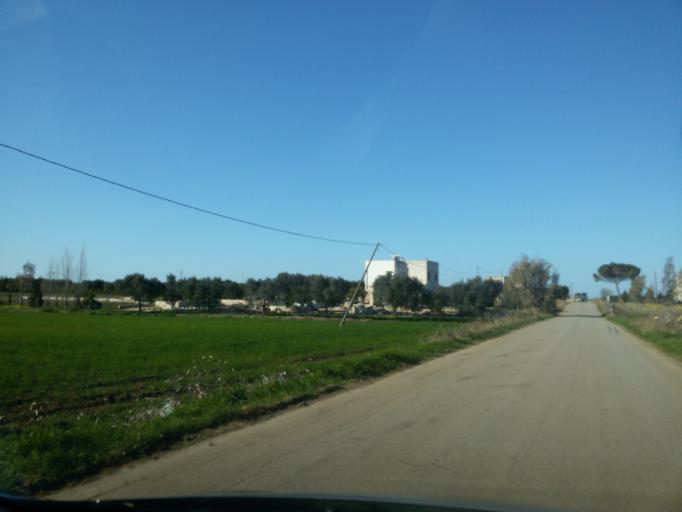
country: IT
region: Apulia
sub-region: Provincia di Brindisi
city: San Vito dei Normanni
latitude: 40.6791
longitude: 17.8214
